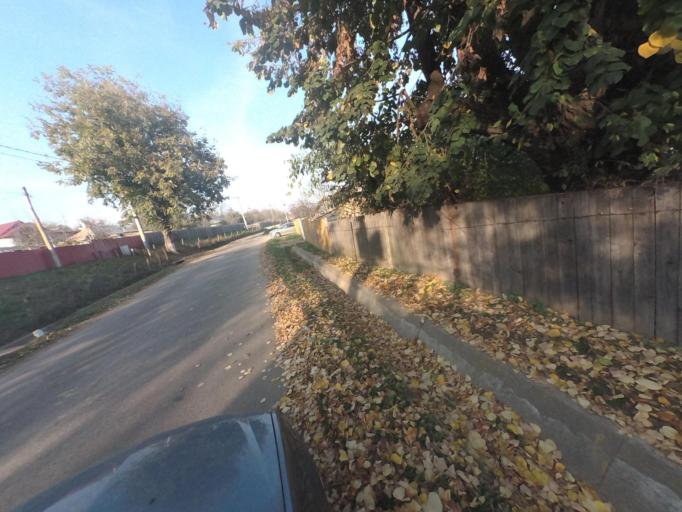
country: RO
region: Vaslui
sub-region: Comuna Bacesti
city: Bacesti
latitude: 46.8226
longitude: 27.2413
